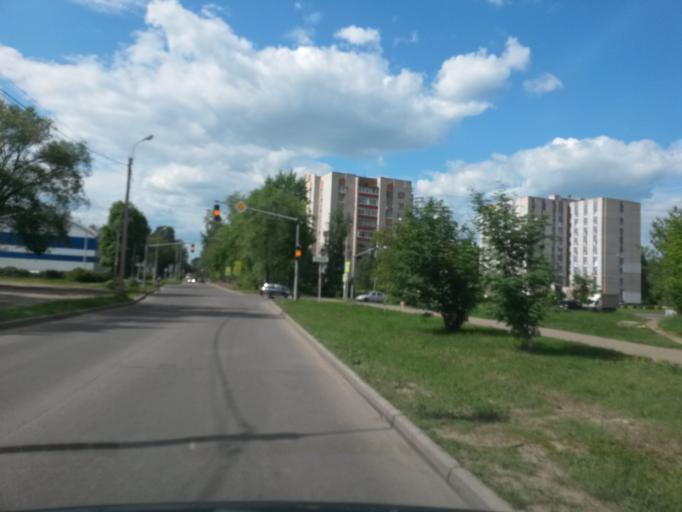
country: RU
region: Jaroslavl
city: Yaroslavl
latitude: 57.6466
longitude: 39.9403
